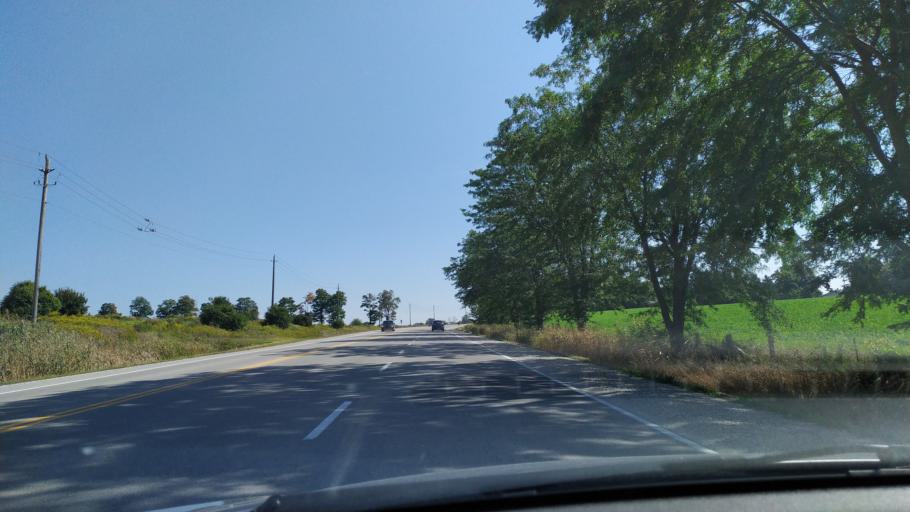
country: CA
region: Ontario
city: Ingersoll
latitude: 43.0660
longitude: -80.8425
